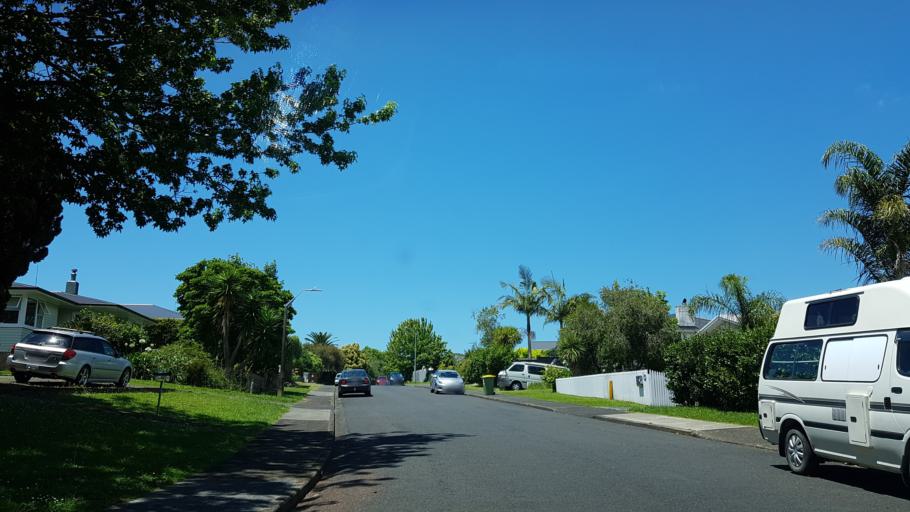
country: NZ
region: Auckland
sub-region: Auckland
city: North Shore
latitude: -36.7858
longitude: 174.6909
